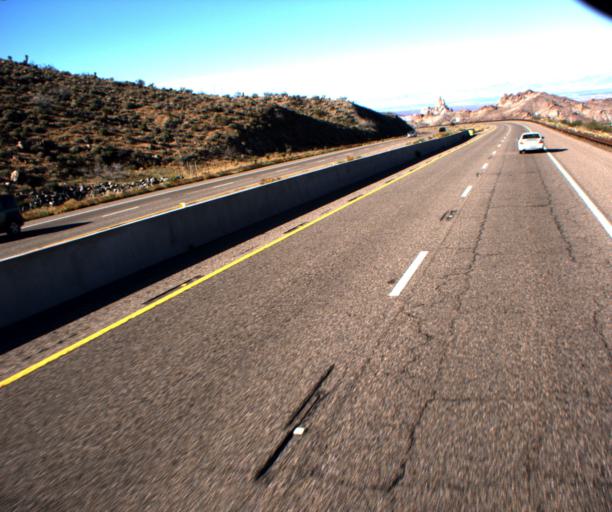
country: US
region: Arizona
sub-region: Mohave County
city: Golden Valley
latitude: 35.2116
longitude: -114.4003
